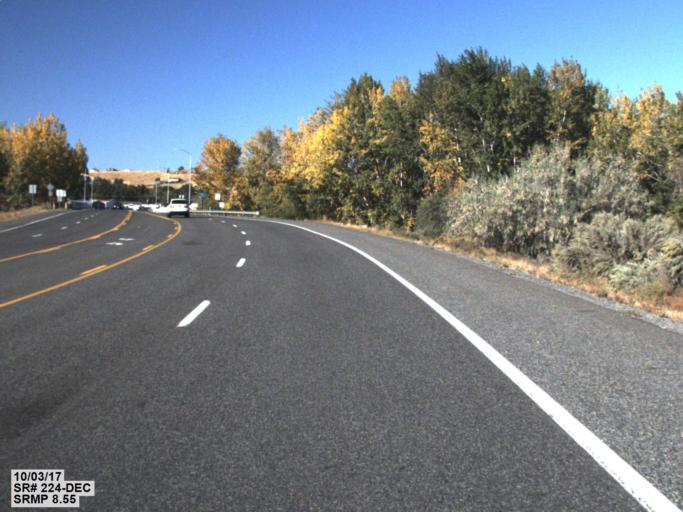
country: US
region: Washington
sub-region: Benton County
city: West Richland
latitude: 46.2982
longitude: -119.3305
